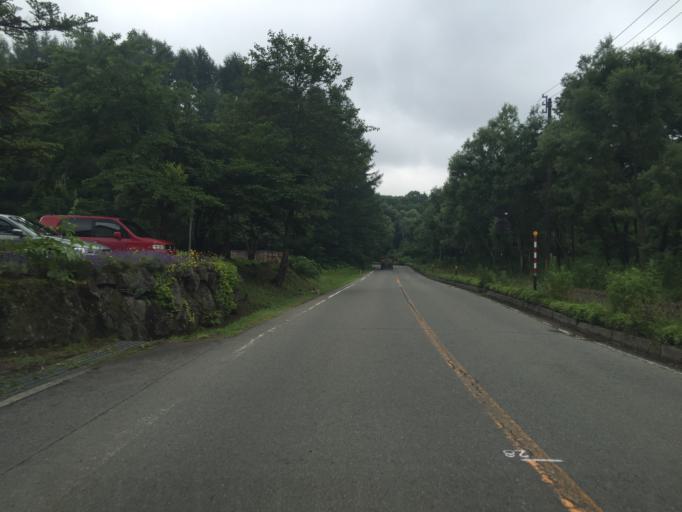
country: JP
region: Fukushima
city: Inawashiro
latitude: 37.6701
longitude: 140.0778
